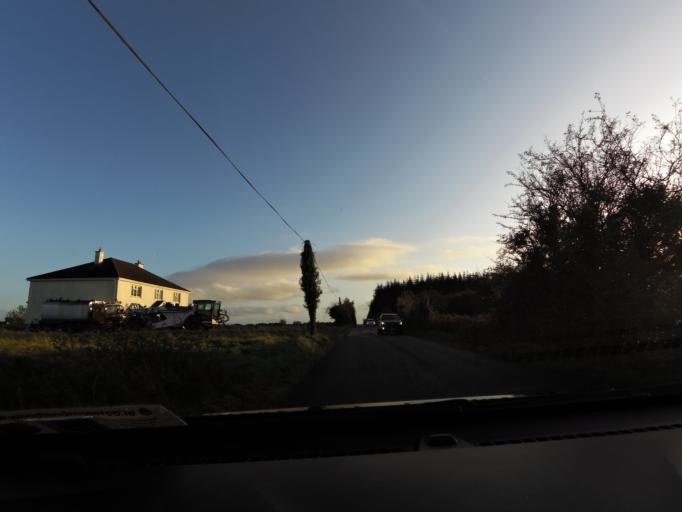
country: IE
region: Connaught
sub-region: Roscommon
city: Castlerea
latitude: 53.6568
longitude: -8.6016
